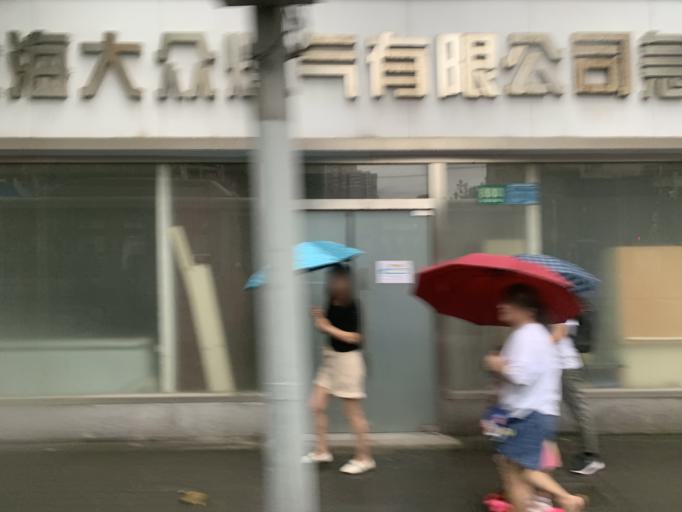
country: CN
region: Shanghai Shi
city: Luwan
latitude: 31.2146
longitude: 121.4888
